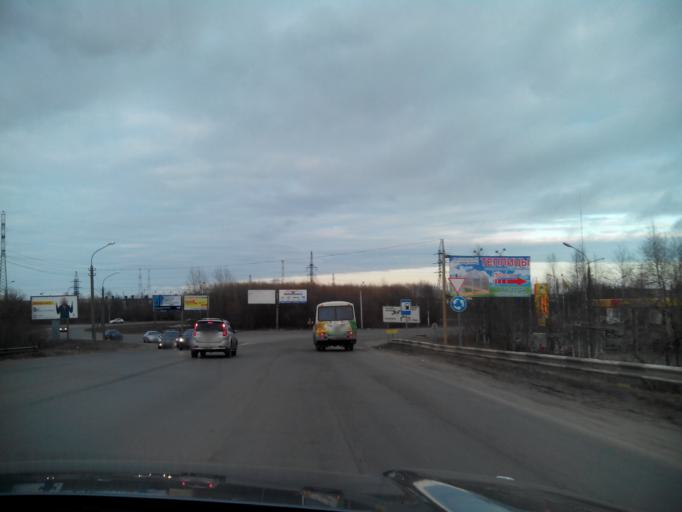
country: RU
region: Arkhangelskaya
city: Arkhangel'sk
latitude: 64.5663
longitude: 40.5646
